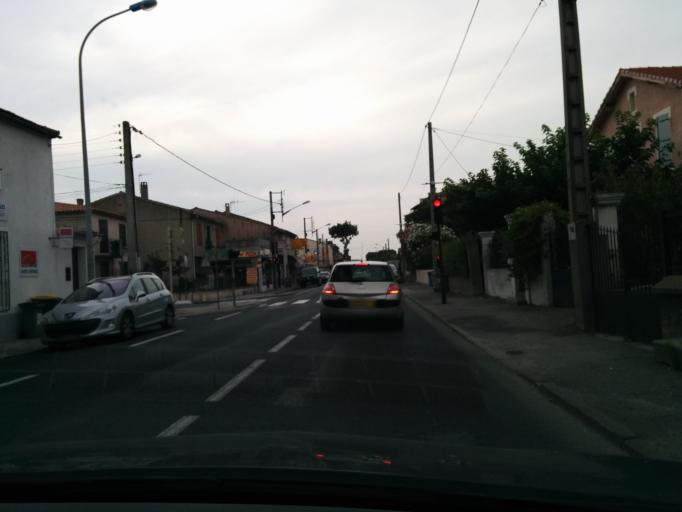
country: FR
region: Languedoc-Roussillon
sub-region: Departement de l'Aude
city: Carcassonne
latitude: 43.2216
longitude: 2.3387
